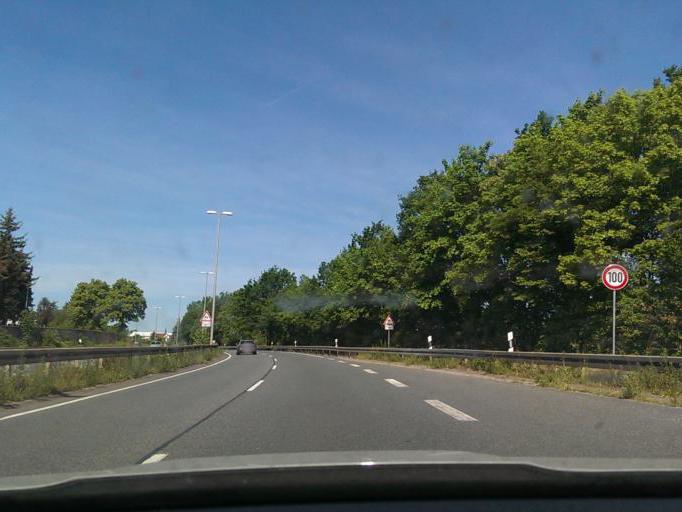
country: DE
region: Lower Saxony
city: Hildesheim
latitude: 52.1563
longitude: 9.9251
